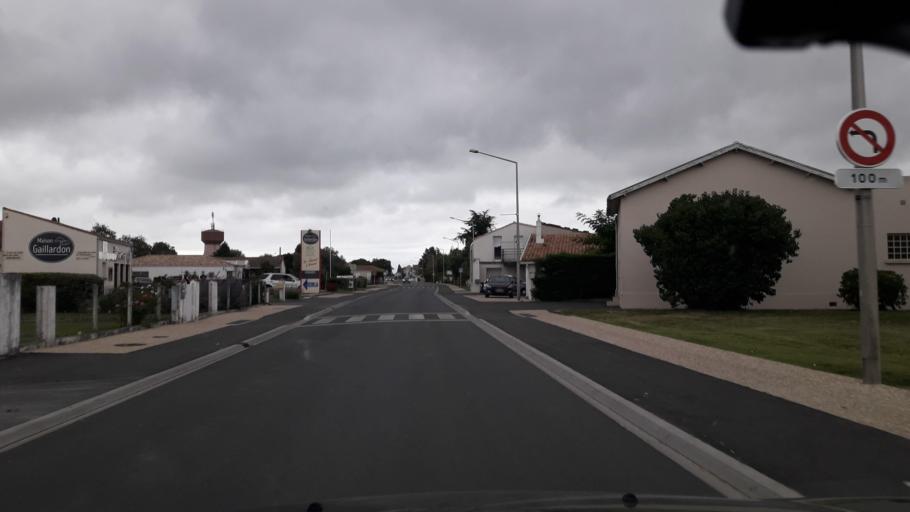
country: FR
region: Poitou-Charentes
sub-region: Departement de la Charente-Maritime
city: Arvert
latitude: 45.7409
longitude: -1.1170
